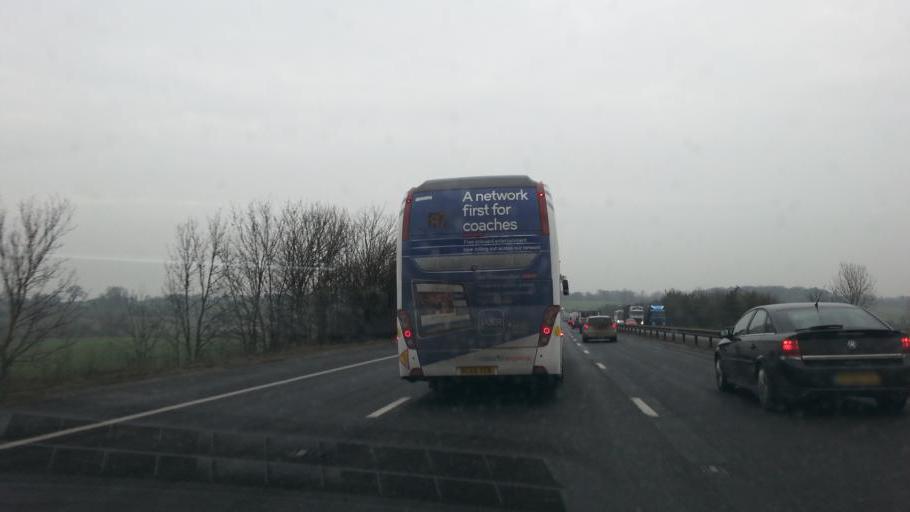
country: GB
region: England
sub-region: Hertfordshire
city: Sawbridgeworth
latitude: 51.7908
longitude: 0.1718
